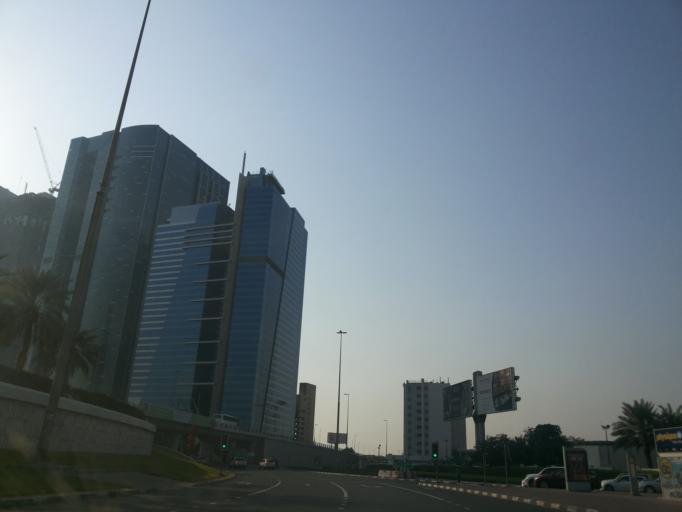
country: AE
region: Ash Shariqah
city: Sharjah
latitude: 25.2304
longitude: 55.2900
